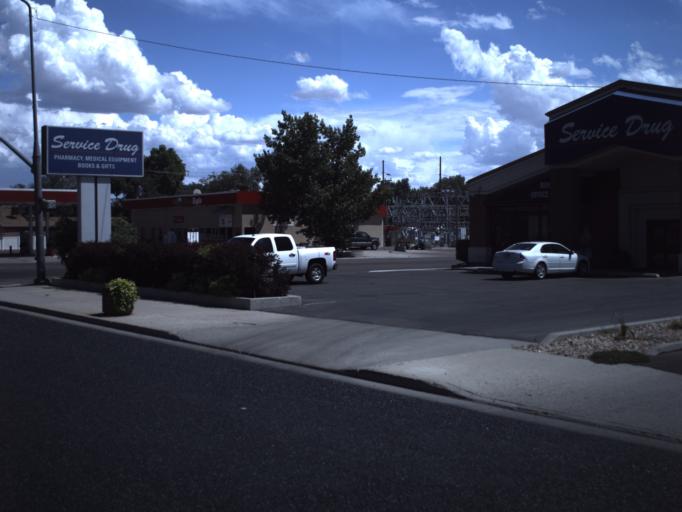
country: US
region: Utah
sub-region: Millard County
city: Delta
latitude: 39.3523
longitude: -112.5799
